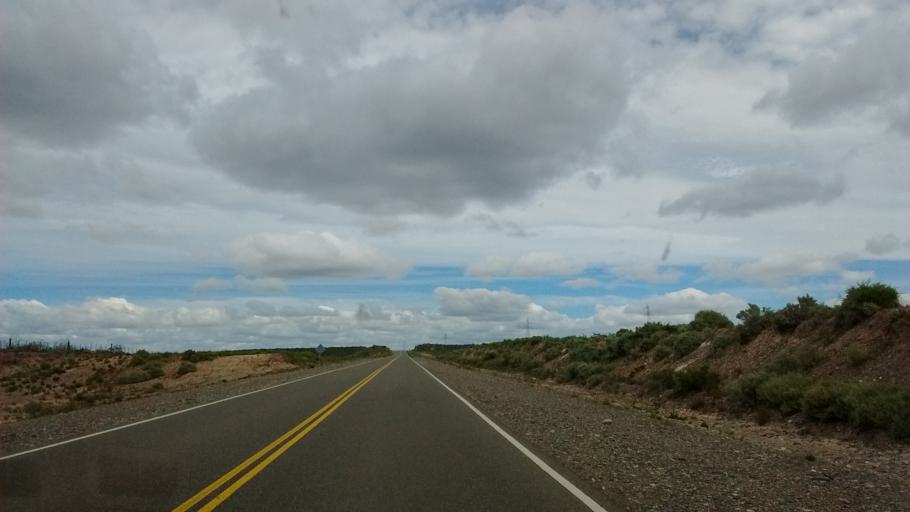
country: AR
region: Neuquen
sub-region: Departamento de Picun Leufu
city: Picun Leufu
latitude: -39.6586
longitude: -69.4193
